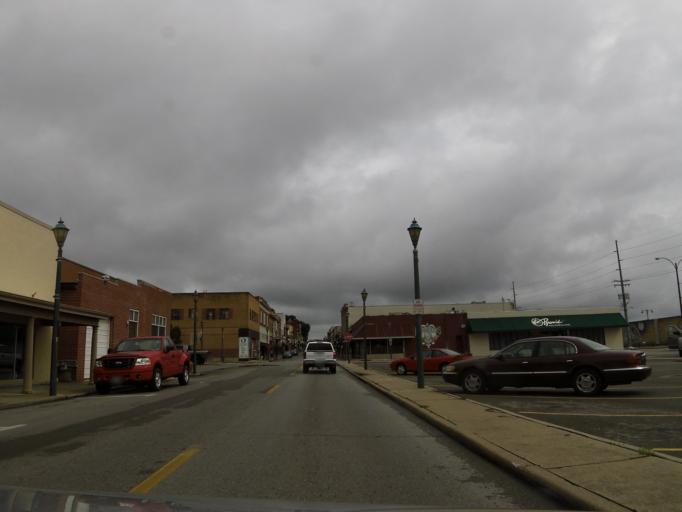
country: US
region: Missouri
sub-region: Cape Girardeau County
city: Cape Girardeau
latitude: 37.3028
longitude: -89.5187
